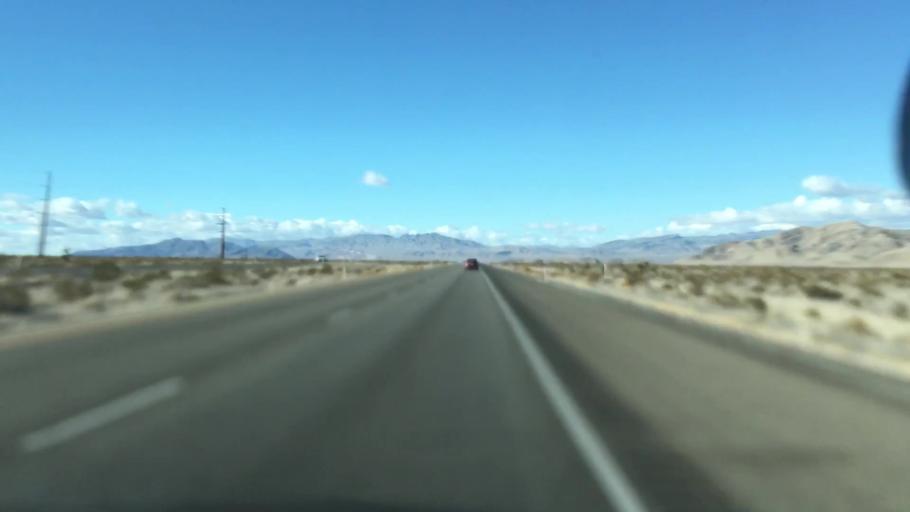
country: US
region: Nevada
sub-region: Nye County
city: Pahrump
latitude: 36.5553
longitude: -115.6025
